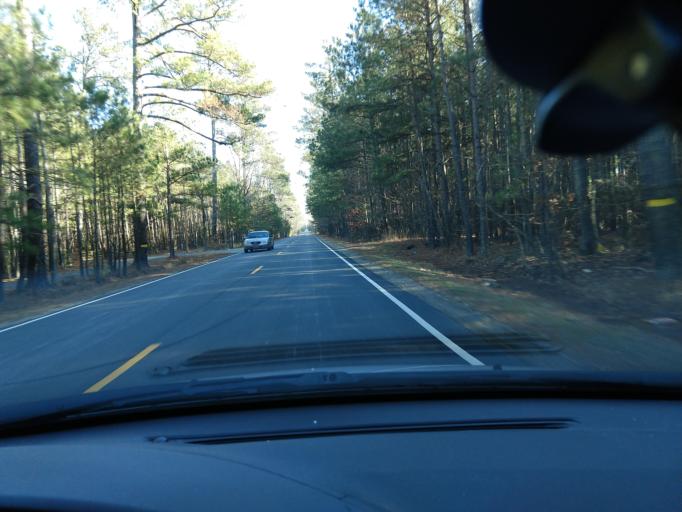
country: US
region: Virginia
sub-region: Surry County
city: Surry
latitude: 37.2791
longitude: -76.9145
